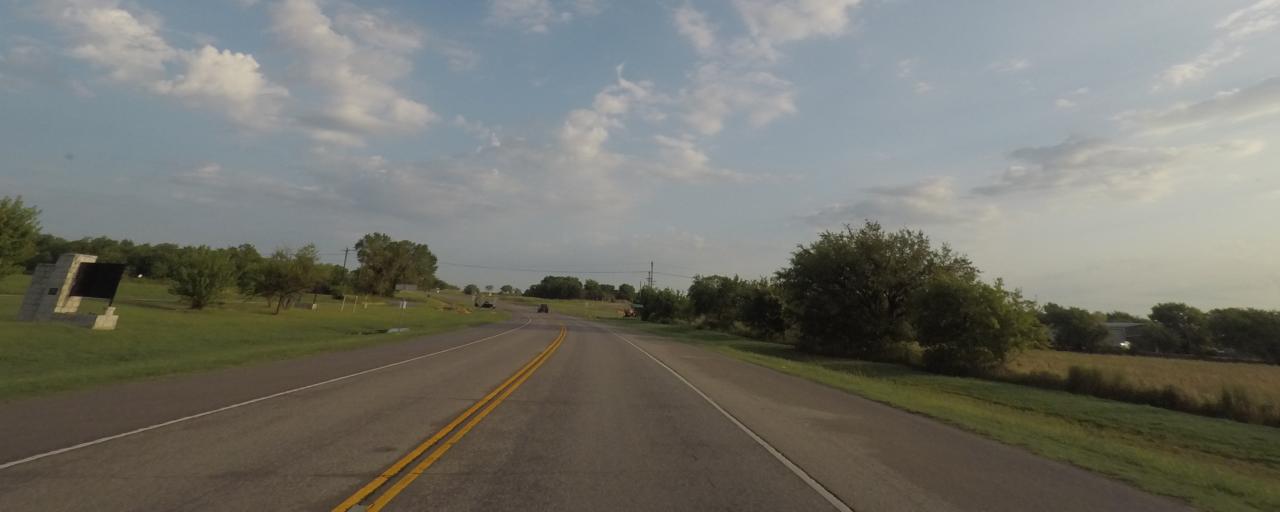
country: US
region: Oklahoma
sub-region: Stephens County
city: Comanche
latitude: 34.3749
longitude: -97.9643
